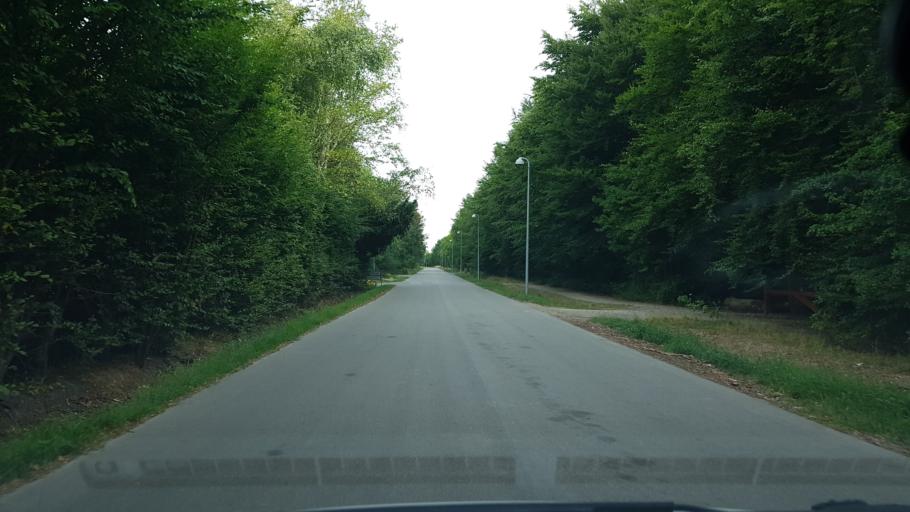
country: DK
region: Capital Region
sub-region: Brondby Kommune
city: Brondbyvester
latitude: 55.6327
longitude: 12.4120
